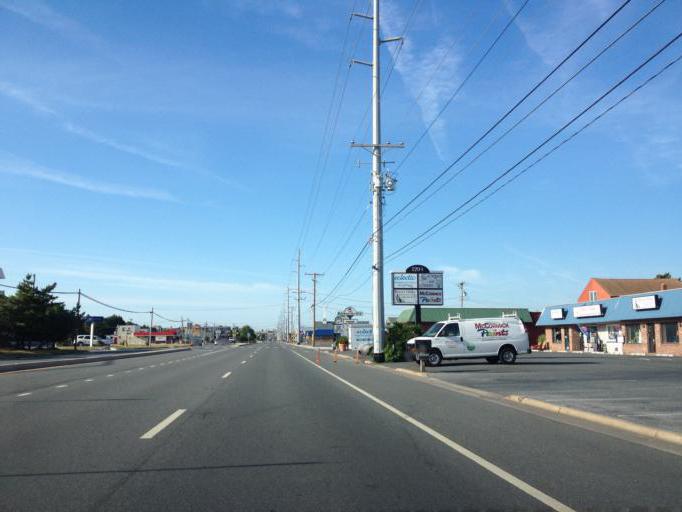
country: US
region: Delaware
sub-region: Sussex County
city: Bethany Beach
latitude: 38.4622
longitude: -75.0521
